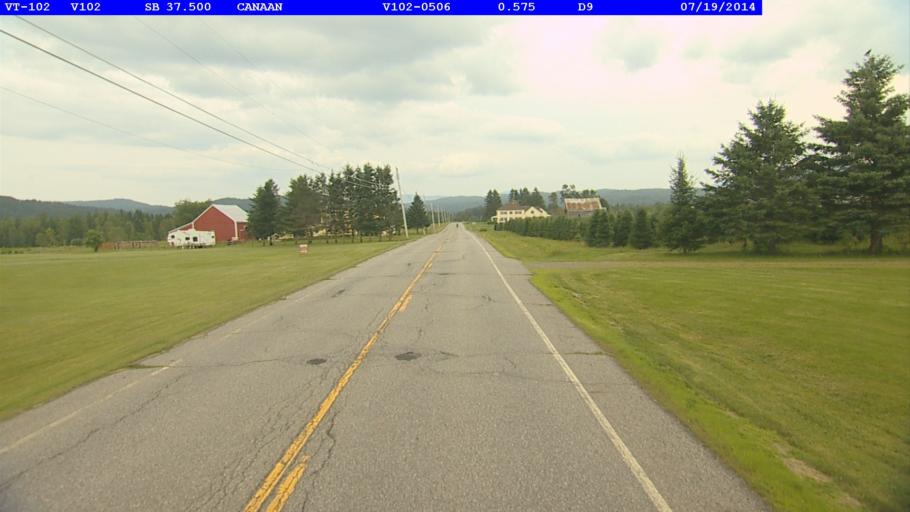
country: US
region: New Hampshire
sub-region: Coos County
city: Colebrook
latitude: 44.9173
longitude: -71.5142
